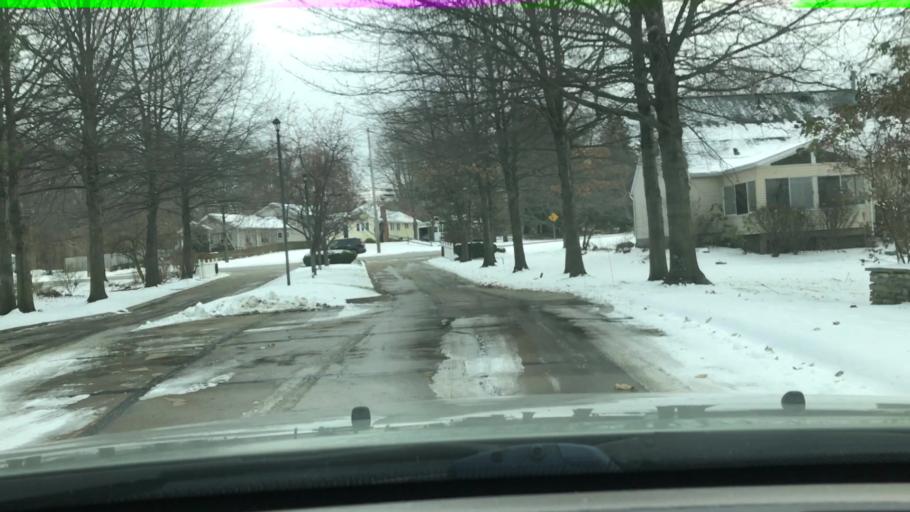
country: US
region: Ohio
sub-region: Lake County
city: Mentor
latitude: 41.6869
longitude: -81.3139
